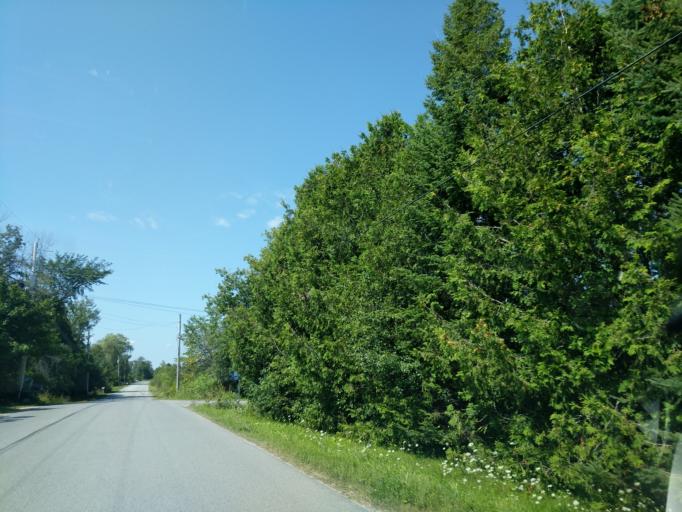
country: CA
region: Ontario
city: Bells Corners
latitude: 45.4464
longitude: -75.9151
